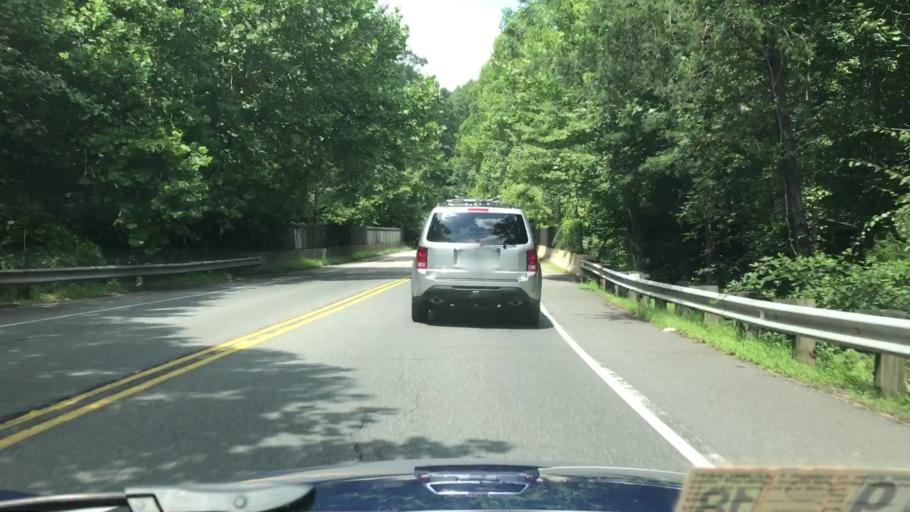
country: US
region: Virginia
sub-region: Fairfax County
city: Wolf Trap
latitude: 38.9232
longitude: -77.3114
